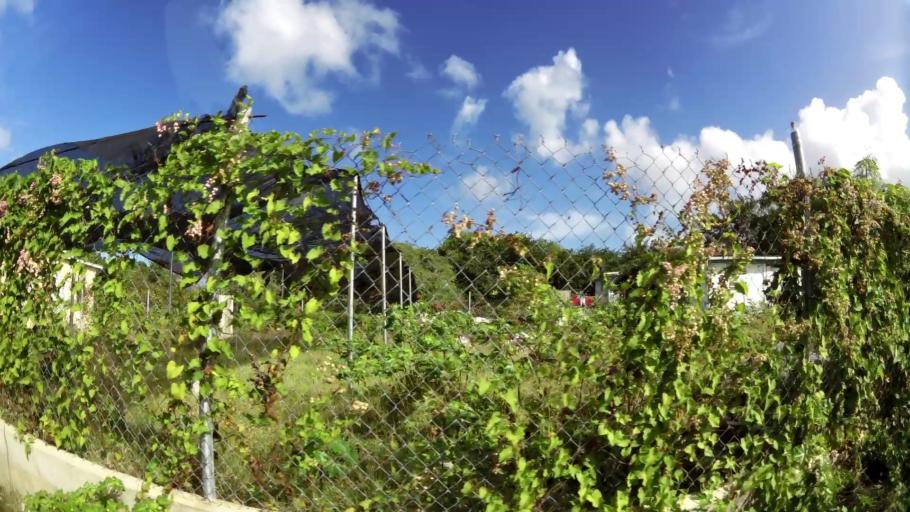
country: KN
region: Saint Paul Charlestown
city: Charlestown
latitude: 17.1294
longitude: -62.6273
